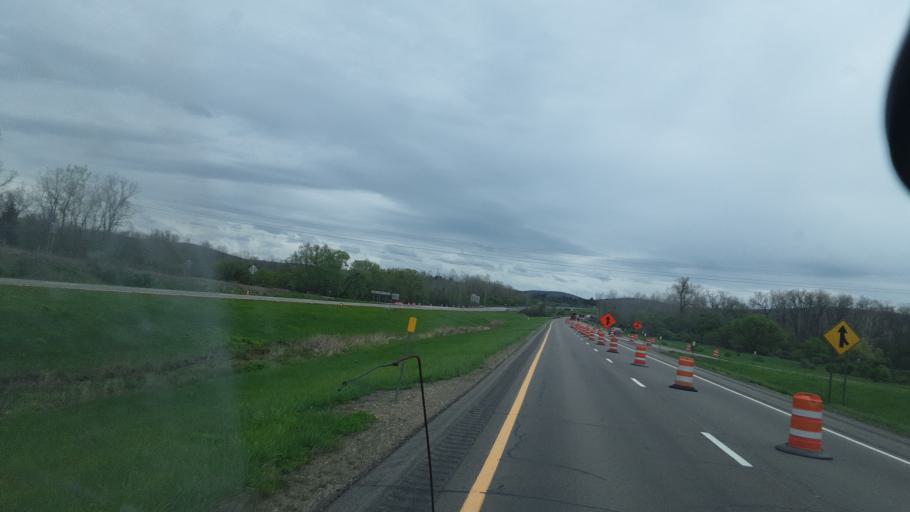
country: US
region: New York
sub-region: Allegany County
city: Belmont
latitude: 42.2609
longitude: -78.0618
